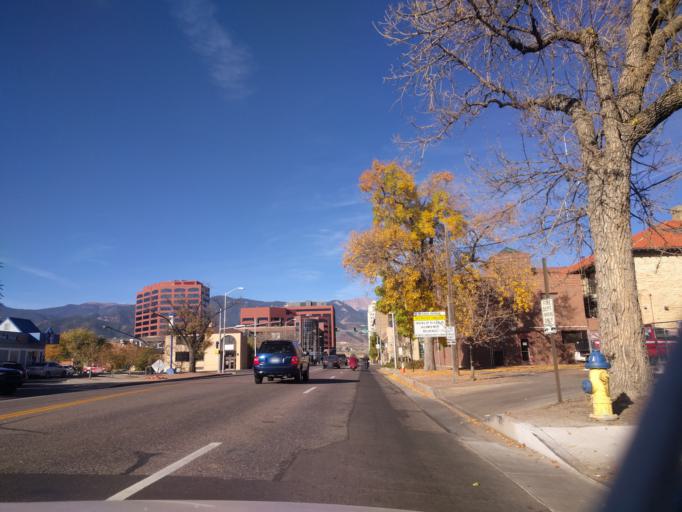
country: US
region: Colorado
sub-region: El Paso County
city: Colorado Springs
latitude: 38.8324
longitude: -104.8190
